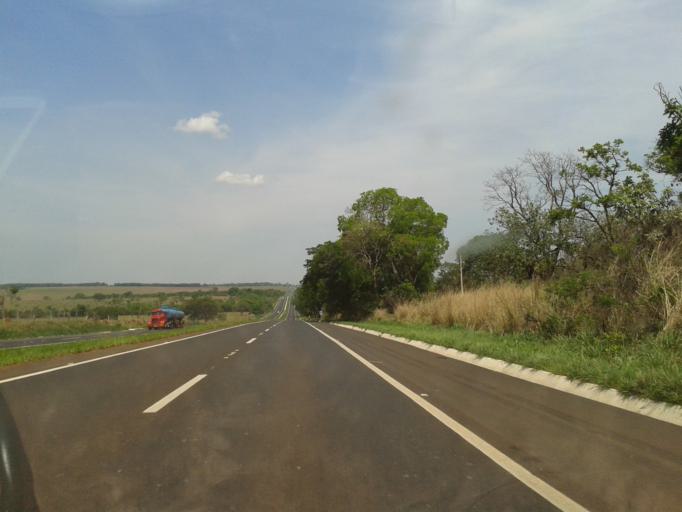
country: BR
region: Minas Gerais
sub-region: Monte Alegre De Minas
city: Monte Alegre de Minas
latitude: -18.8552
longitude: -48.7773
